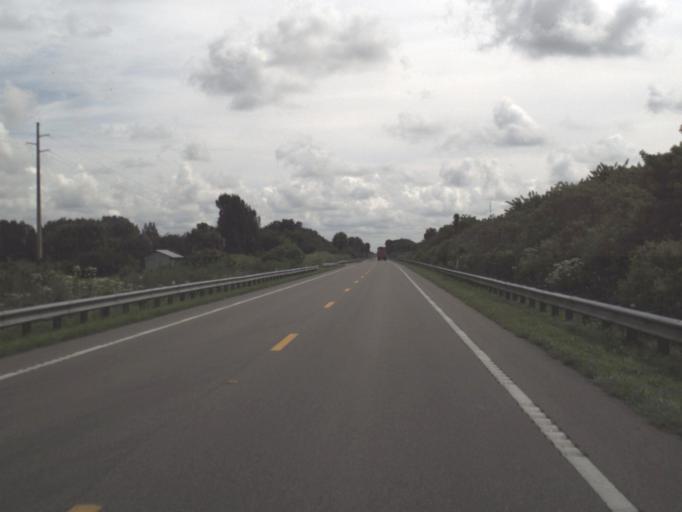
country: US
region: Florida
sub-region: Highlands County
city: Lake Placid
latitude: 27.2092
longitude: -81.1876
